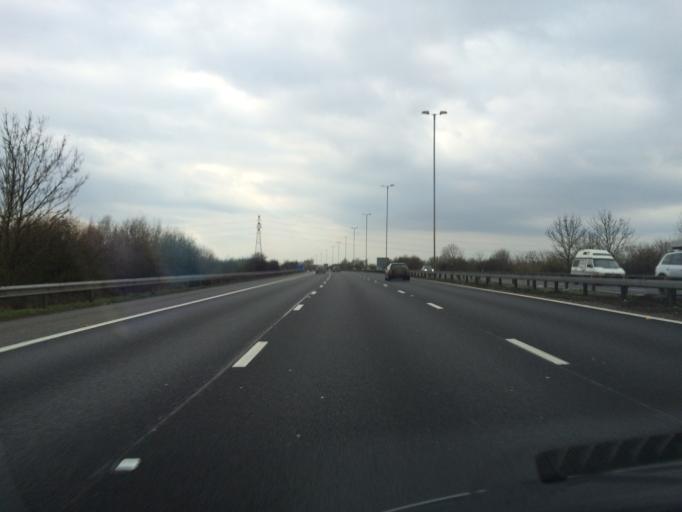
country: GB
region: England
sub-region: Reading
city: Reading
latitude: 51.4194
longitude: -0.9962
